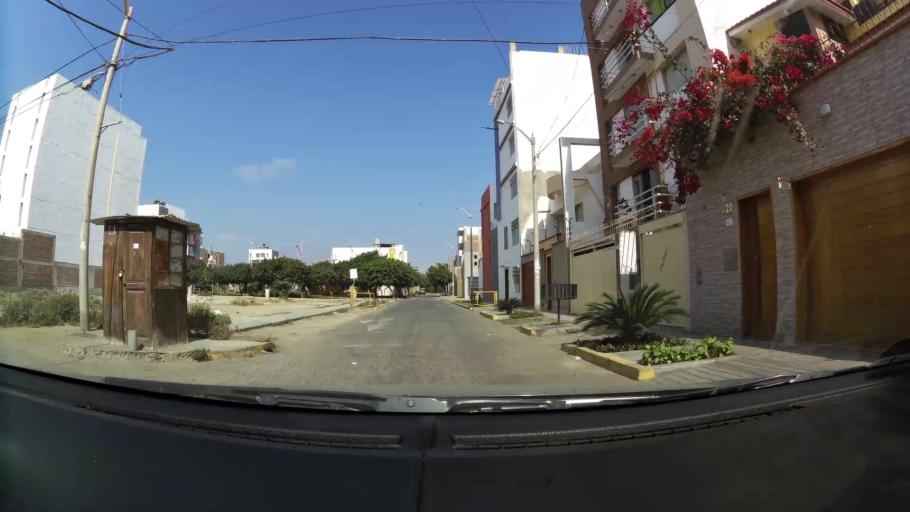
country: PE
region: La Libertad
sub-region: Provincia de Trujillo
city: Trujillo
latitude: -8.1289
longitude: -79.0296
